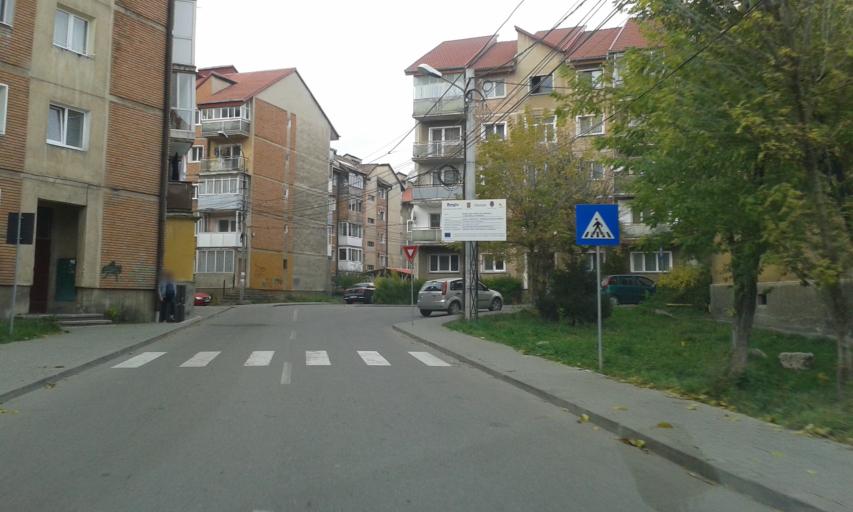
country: RO
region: Hunedoara
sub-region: Municipiul Petrosani
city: Petrosani
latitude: 45.4203
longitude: 23.3728
